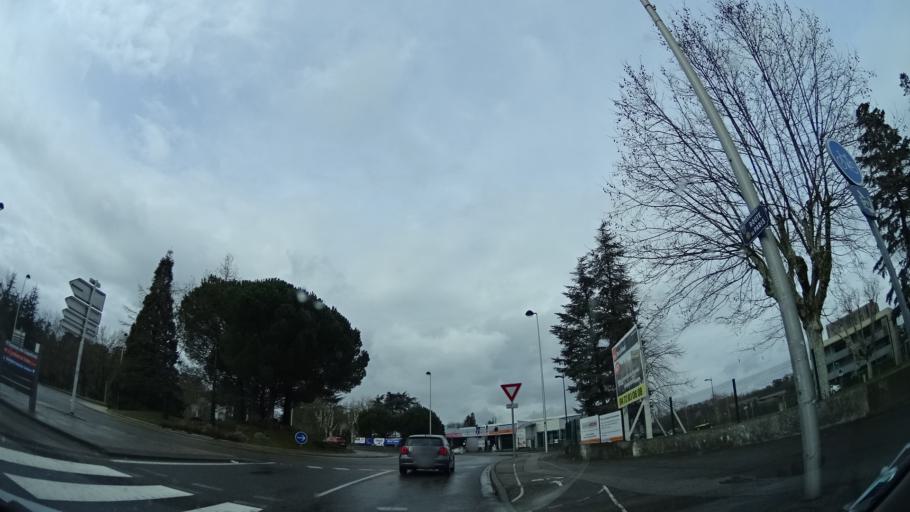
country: FR
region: Rhone-Alpes
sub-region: Departement du Rhone
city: Charbonnieres-les-Bains
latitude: 45.7697
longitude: 4.7571
